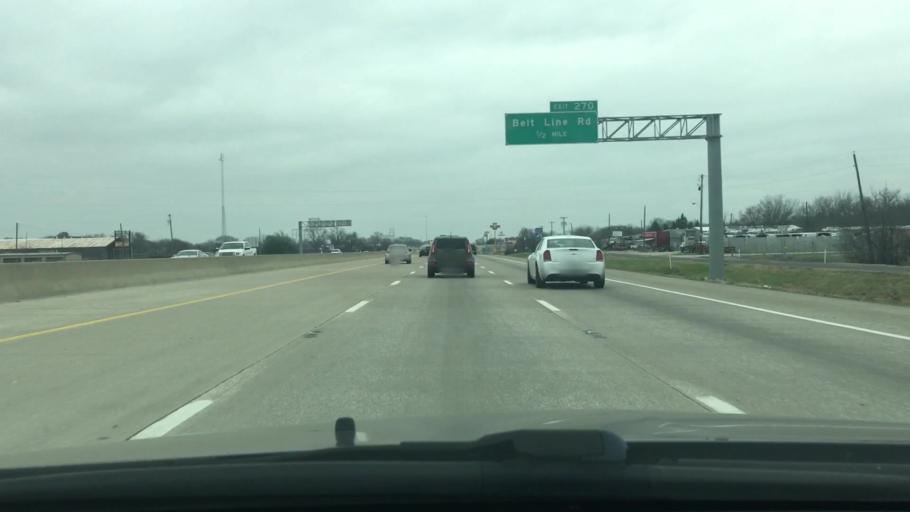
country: US
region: Texas
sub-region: Dallas County
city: Wilmer
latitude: 32.6013
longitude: -96.6846
